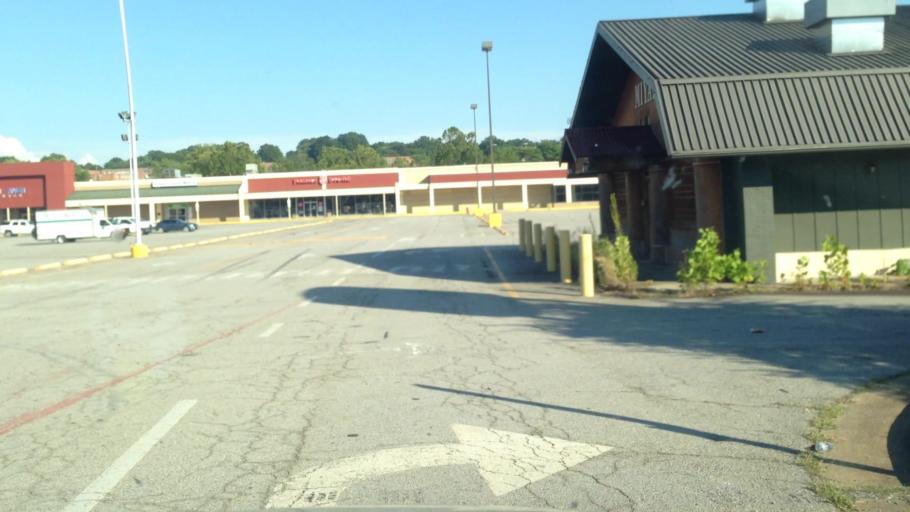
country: US
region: Virginia
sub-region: City of Danville
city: Danville
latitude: 36.5893
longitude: -79.4186
